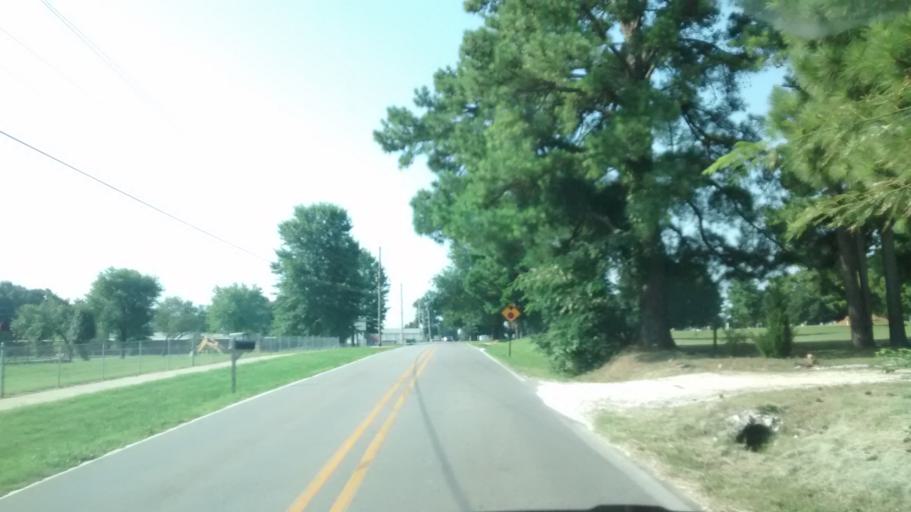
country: US
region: Arkansas
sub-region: Washington County
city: Farmington
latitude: 36.0448
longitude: -94.2540
